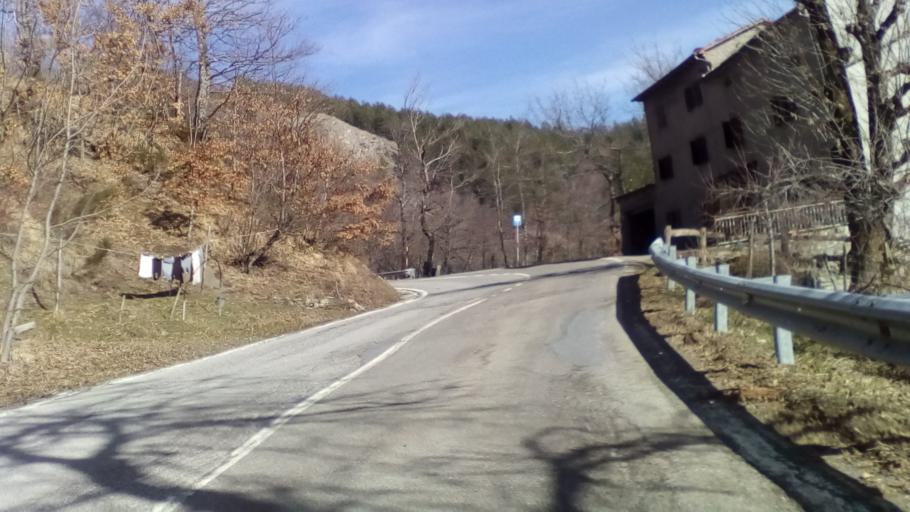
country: IT
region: Emilia-Romagna
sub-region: Provincia di Modena
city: Pievepelago
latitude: 44.2212
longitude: 10.6233
